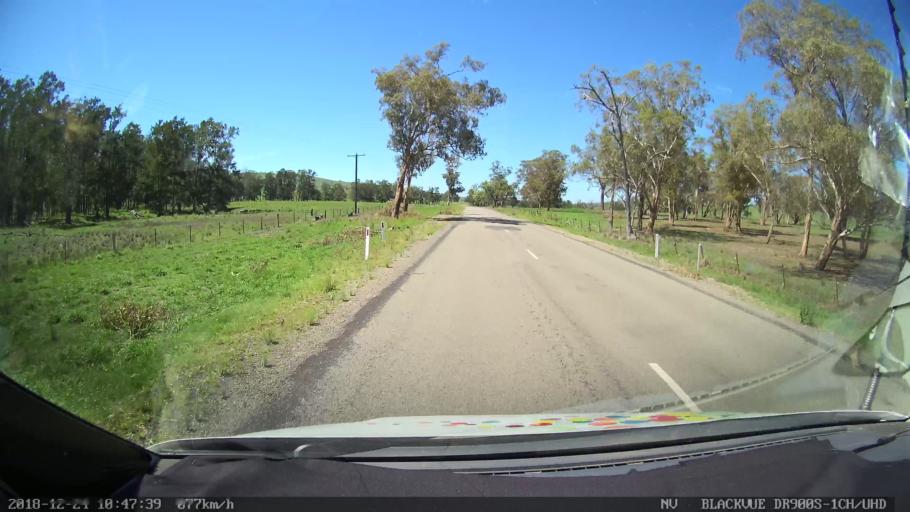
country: AU
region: New South Wales
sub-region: Upper Hunter Shire
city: Merriwa
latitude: -31.9267
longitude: 150.4297
